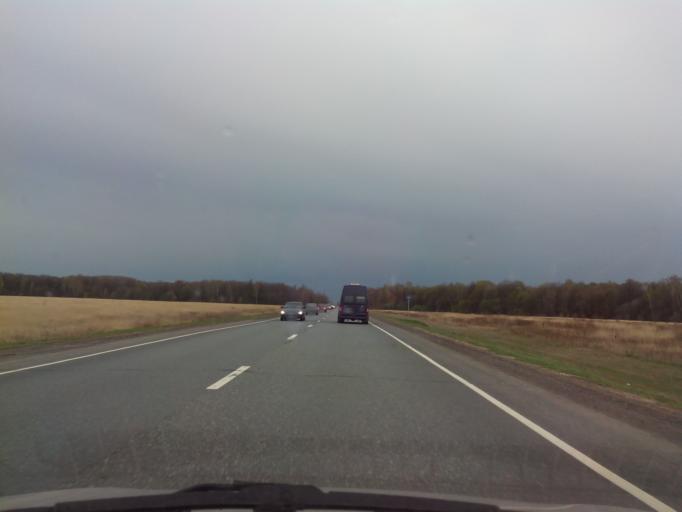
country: RU
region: Moskovskaya
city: Uzunovo
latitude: 54.5614
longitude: 38.4585
